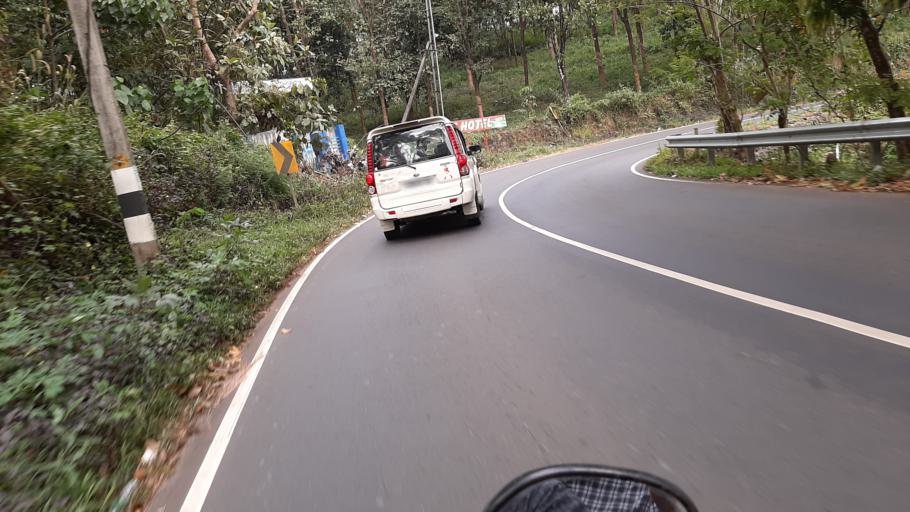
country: IN
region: Kerala
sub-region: Pattanamtitta
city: Pathanamthitta
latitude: 9.4535
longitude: 76.8680
